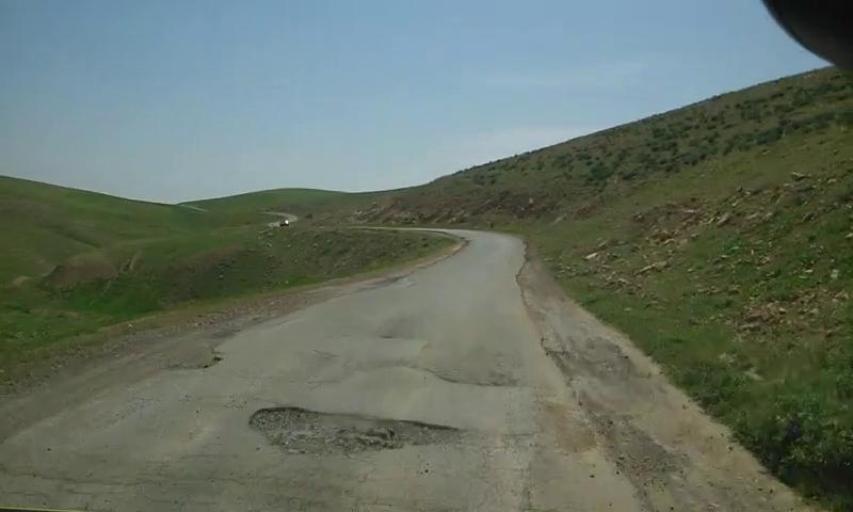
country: PS
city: `Arab ar Rashaydah
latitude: 31.5550
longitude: 35.2492
